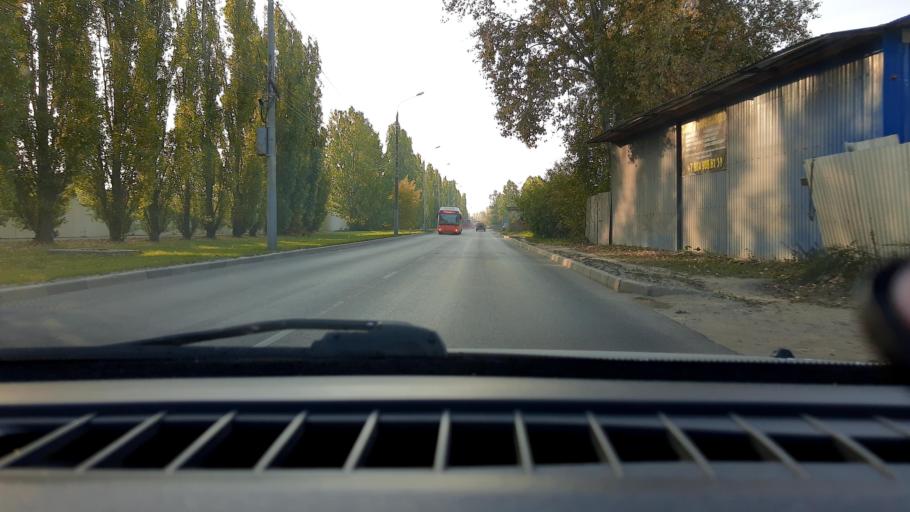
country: RU
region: Nizjnij Novgorod
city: Gorbatovka
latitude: 56.3492
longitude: 43.8037
